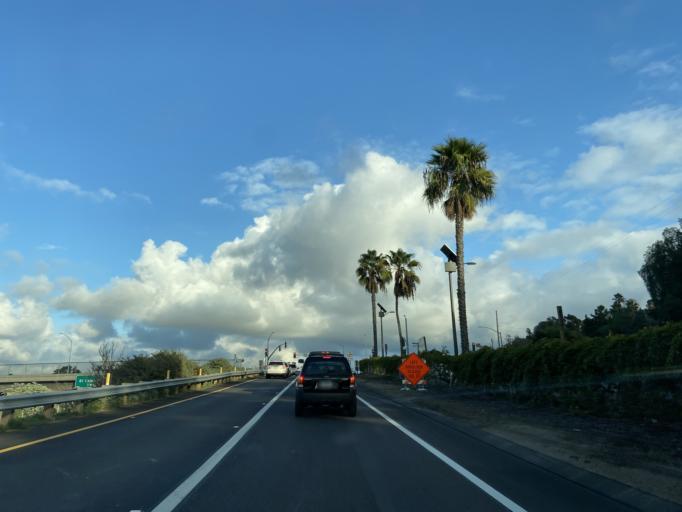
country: US
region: California
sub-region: San Diego County
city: La Mesa
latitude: 32.7788
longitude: -116.9984
